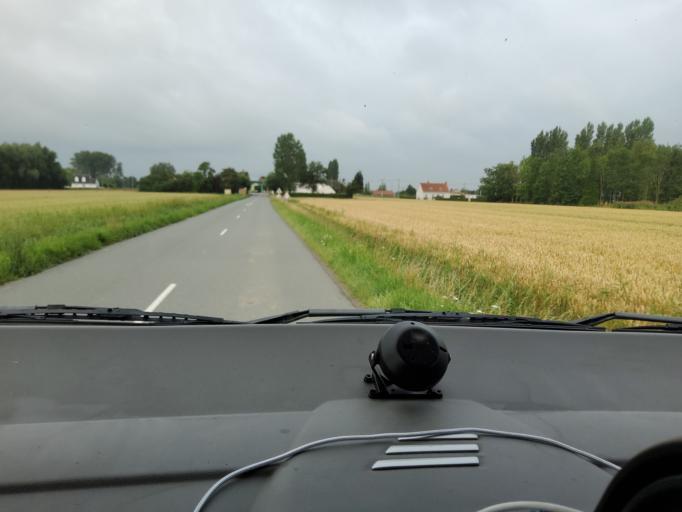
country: FR
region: Nord-Pas-de-Calais
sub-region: Departement du Pas-de-Calais
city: Sainte-Marie-Kerque
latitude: 50.9199
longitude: 2.1639
